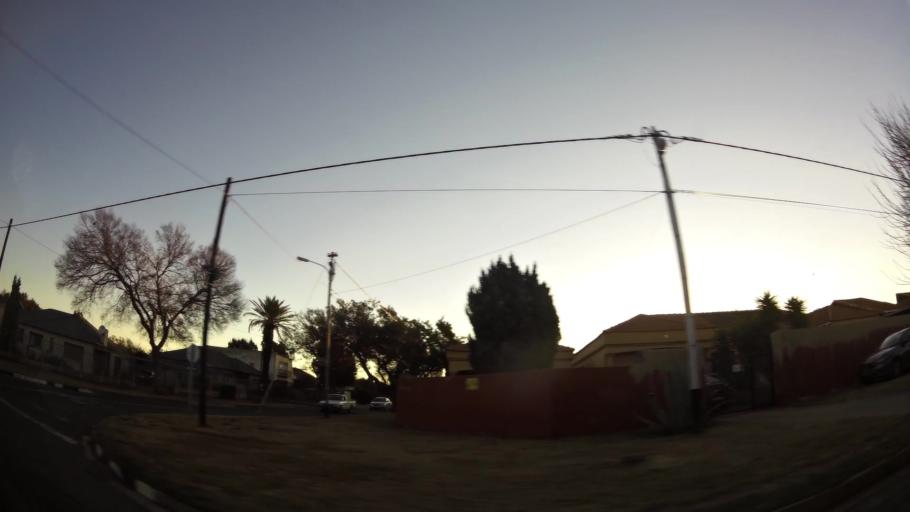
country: ZA
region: Gauteng
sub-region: City of Johannesburg Metropolitan Municipality
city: Roodepoort
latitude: -26.1521
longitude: 27.8817
